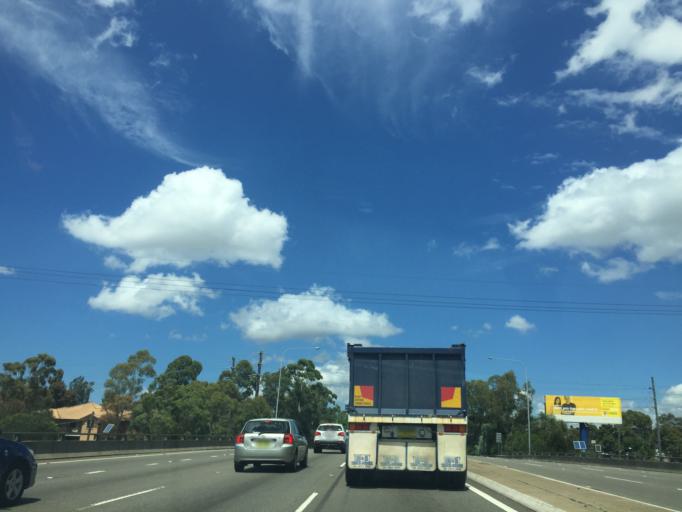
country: AU
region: New South Wales
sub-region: Strathfield
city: Homebush
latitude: -33.8637
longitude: 151.0665
